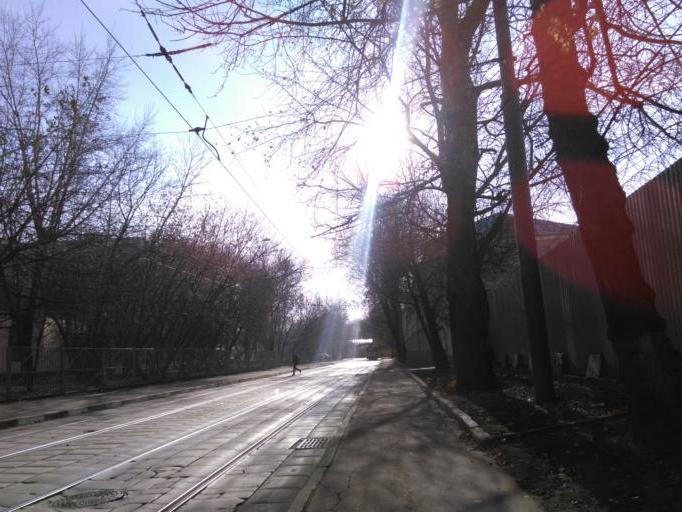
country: RU
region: Moscow
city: Novyye Cheremushki
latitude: 55.7081
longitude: 37.6106
